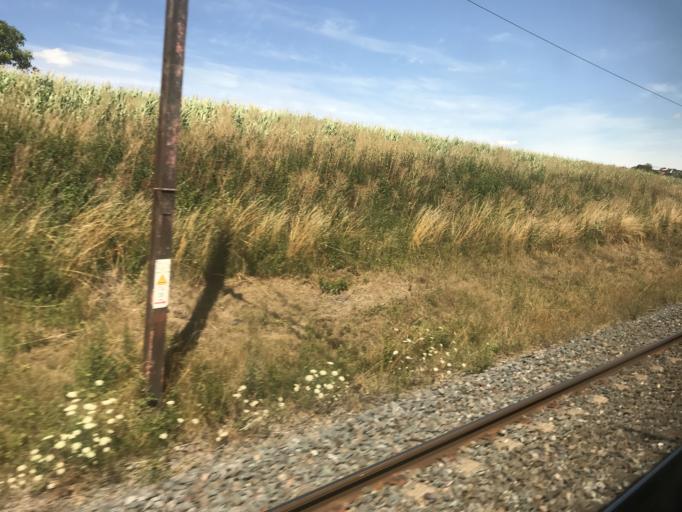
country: FR
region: Lorraine
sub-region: Departement de la Moselle
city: Sarrebourg
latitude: 48.7888
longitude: 7.0272
